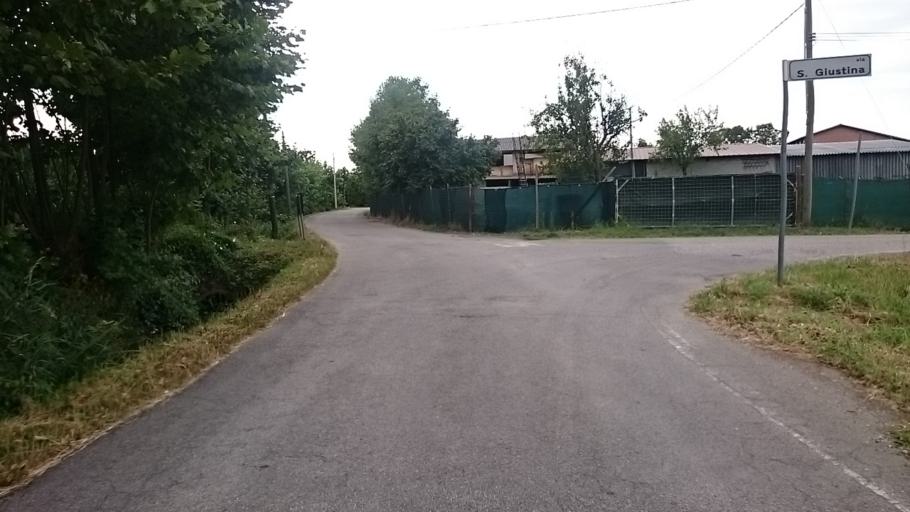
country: IT
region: Veneto
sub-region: Provincia di Padova
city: Terradura
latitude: 45.3283
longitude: 11.8298
